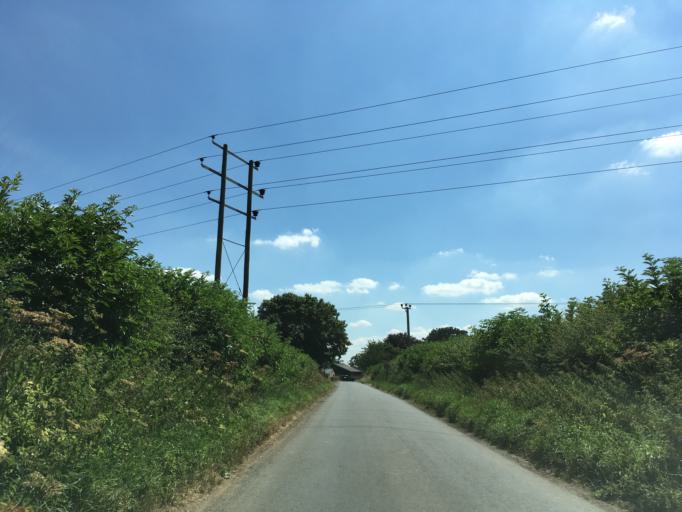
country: GB
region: England
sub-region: Gloucestershire
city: Tetbury
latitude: 51.6355
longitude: -2.1321
